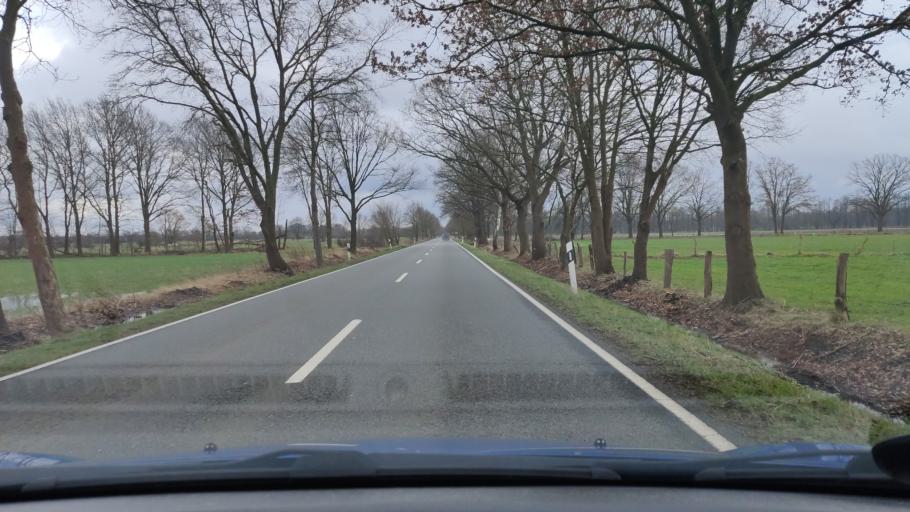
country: DE
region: Lower Saxony
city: Garbsen-Mitte
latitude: 52.4660
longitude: 9.6438
